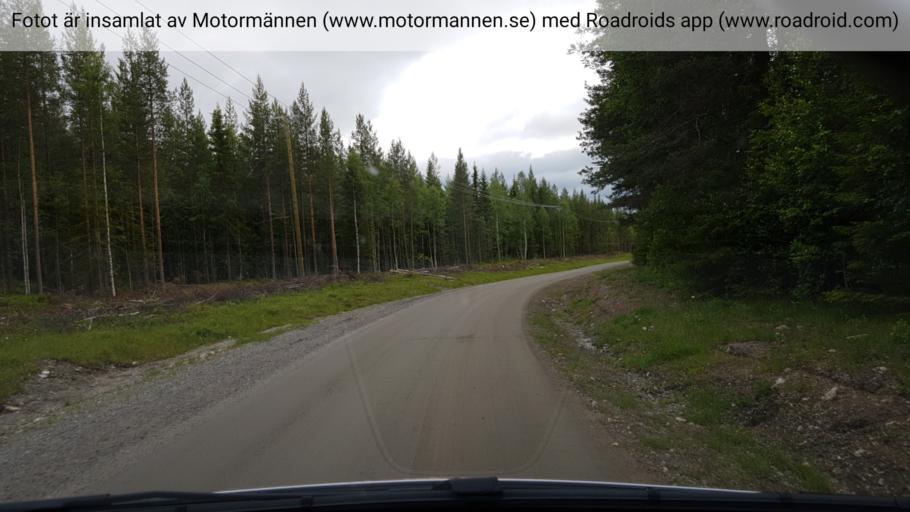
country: SE
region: Vaesterbotten
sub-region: Lycksele Kommun
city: Lycksele
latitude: 64.5253
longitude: 19.0066
